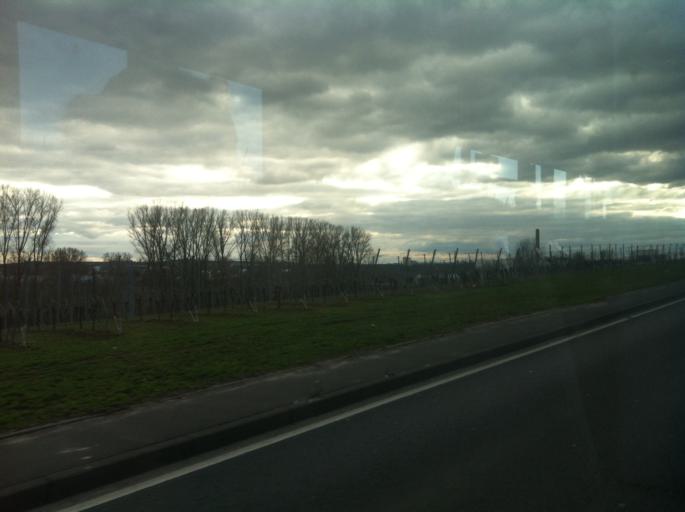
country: DE
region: Hesse
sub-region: Regierungsbezirk Darmstadt
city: Hochheim am Main
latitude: 50.0075
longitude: 8.3246
